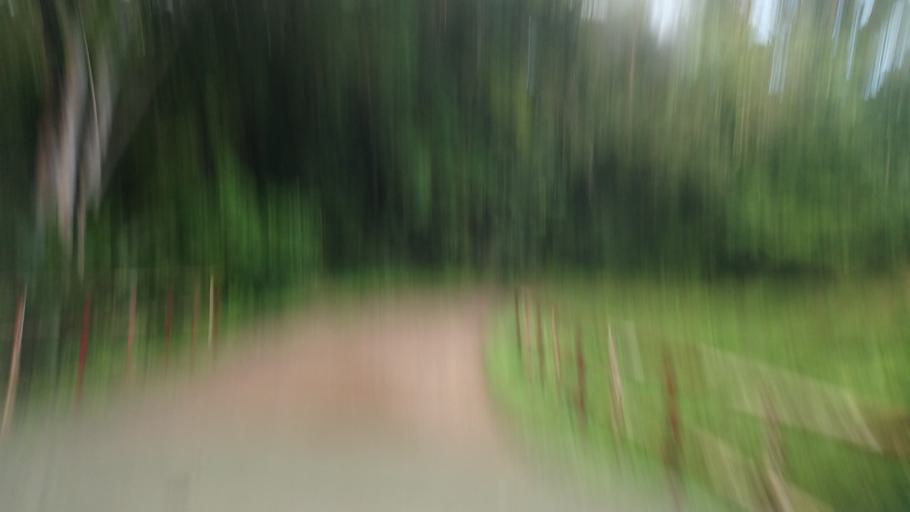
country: TT
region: Couva-Tabaquite-Talparo
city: Tabaquite
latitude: 10.4818
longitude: -61.2098
